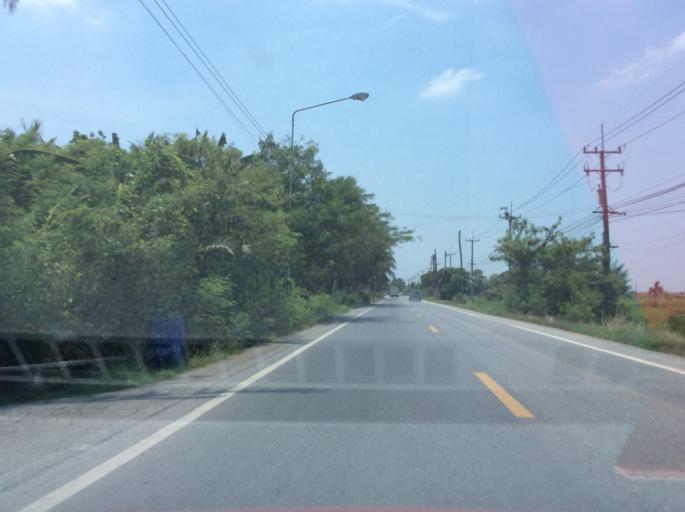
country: TH
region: Pathum Thani
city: Ban Lam Luk Ka
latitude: 14.0006
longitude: 100.7787
